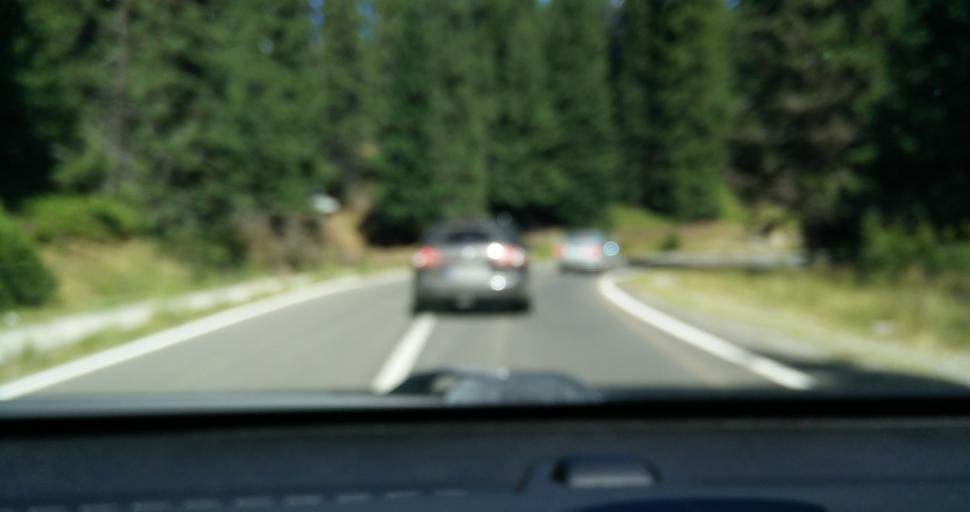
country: RO
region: Hunedoara
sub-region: Oras Petrila
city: Petrila
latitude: 45.4719
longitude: 23.6325
